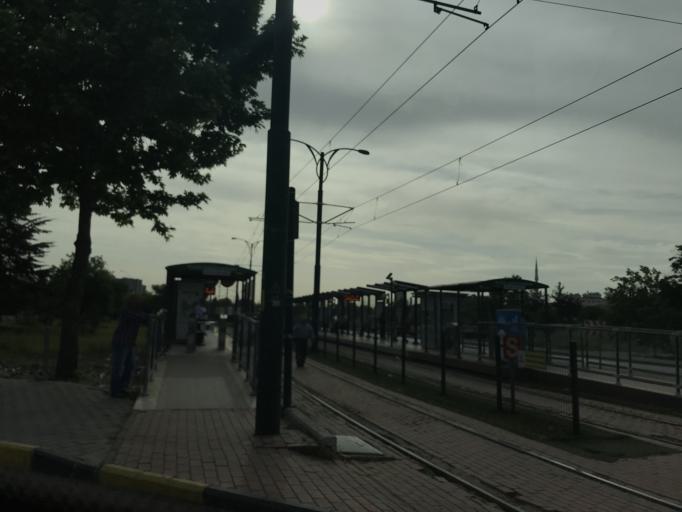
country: TR
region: Gaziantep
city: Sahinbey
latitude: 37.0617
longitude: 37.3341
